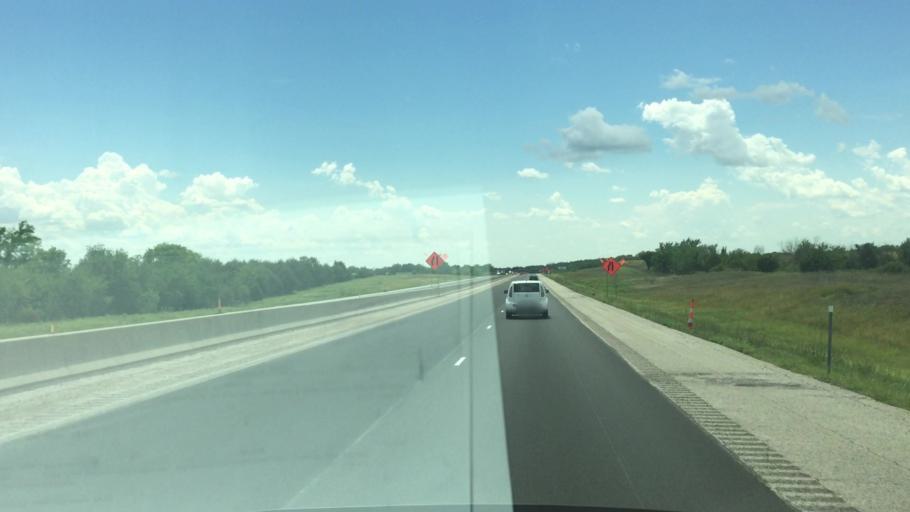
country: US
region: Kansas
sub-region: Osage County
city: Osage City
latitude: 38.7164
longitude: -95.9743
